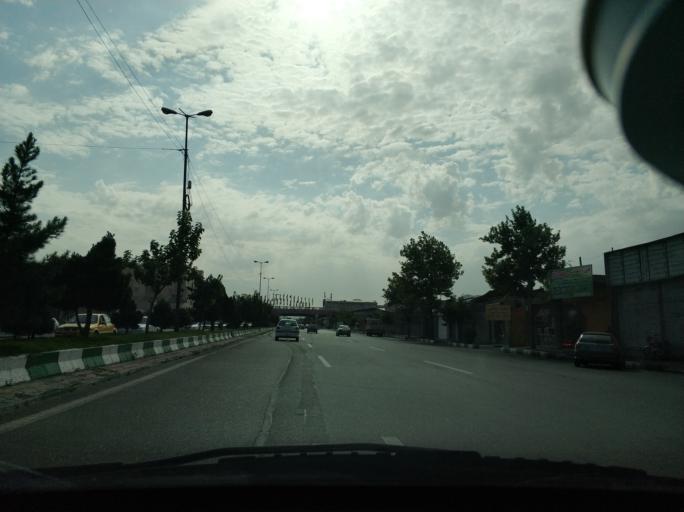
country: IR
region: Tehran
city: Tehran
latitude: 35.7246
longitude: 51.5351
